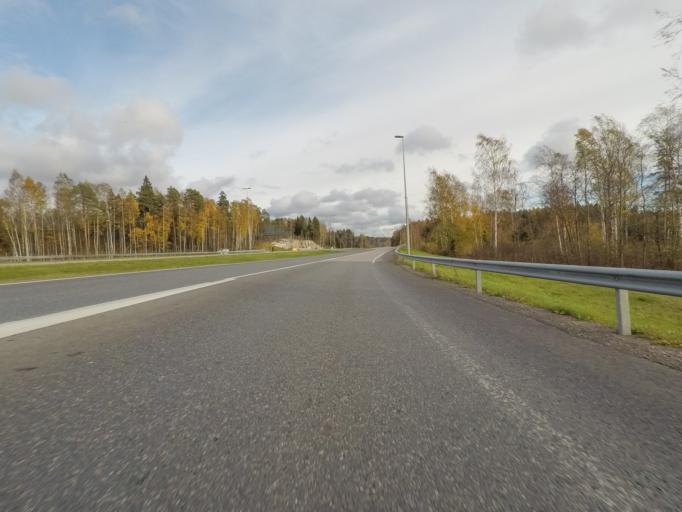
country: FI
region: Uusimaa
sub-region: Helsinki
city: Vantaa
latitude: 60.2578
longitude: 25.1307
